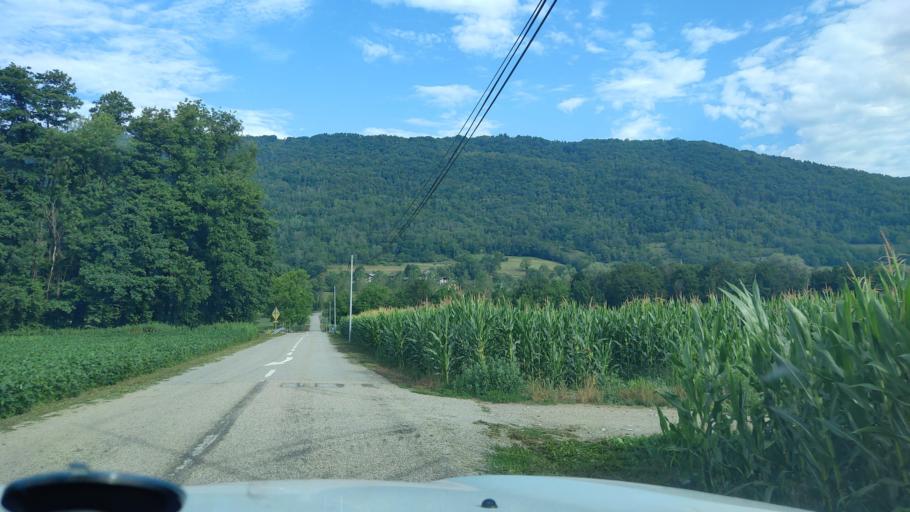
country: FR
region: Rhone-Alpes
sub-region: Departement de la Savoie
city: Coise-Saint-Jean-Pied-Gauthier
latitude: 45.4918
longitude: 6.1516
